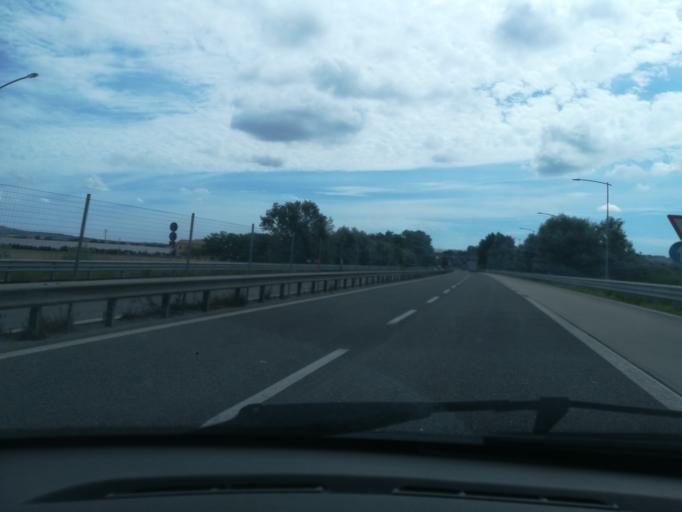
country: IT
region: The Marches
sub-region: Provincia di Macerata
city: Villa San Filippo
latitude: 43.2625
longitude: 13.5652
